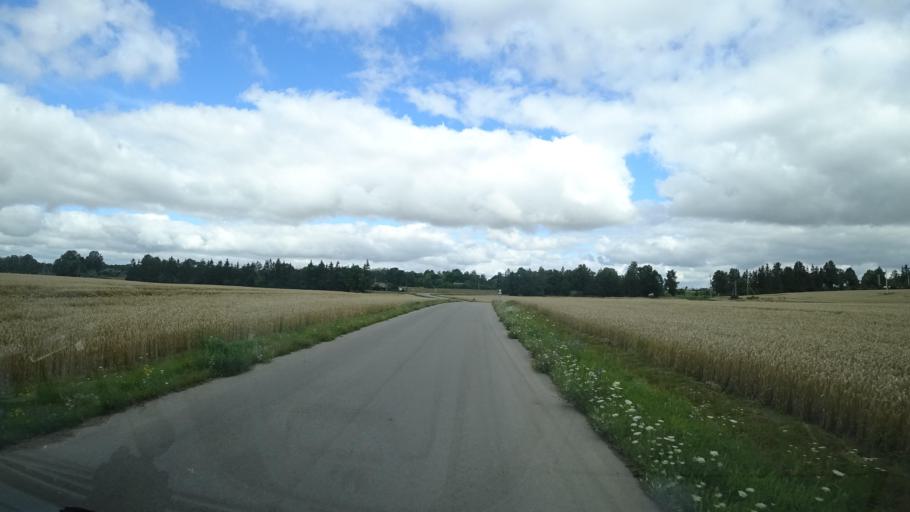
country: LT
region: Marijampoles apskritis
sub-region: Marijampole Municipality
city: Marijampole
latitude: 54.5194
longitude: 23.3212
